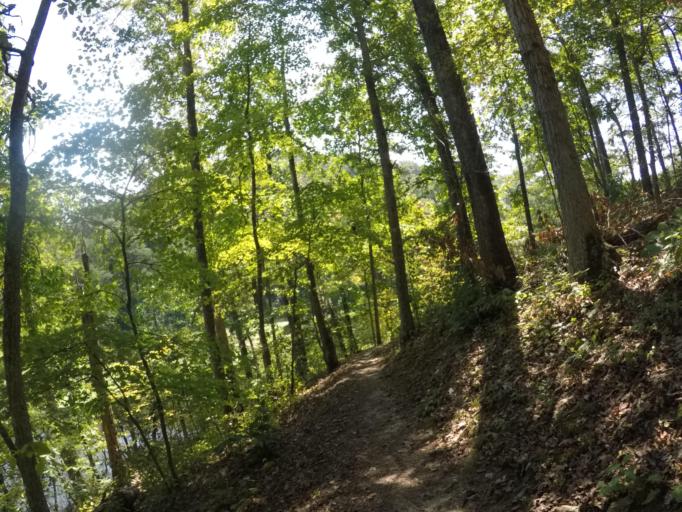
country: US
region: Ohio
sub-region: Lawrence County
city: Ironton
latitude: 38.6189
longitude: -82.6236
